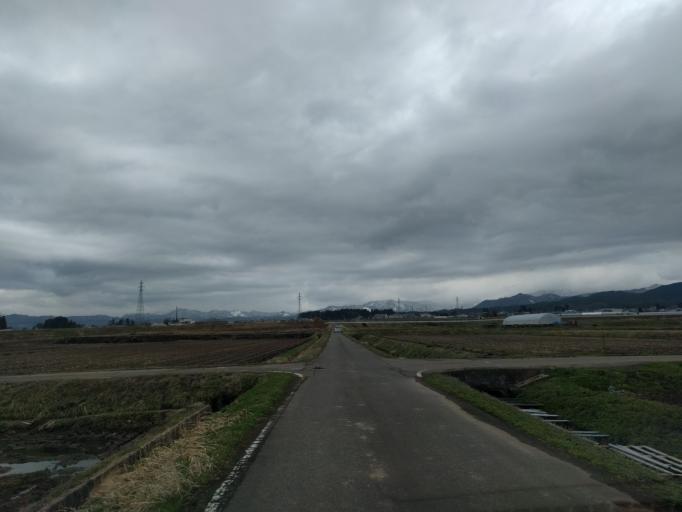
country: JP
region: Fukushima
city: Kitakata
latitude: 37.6496
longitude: 139.9153
